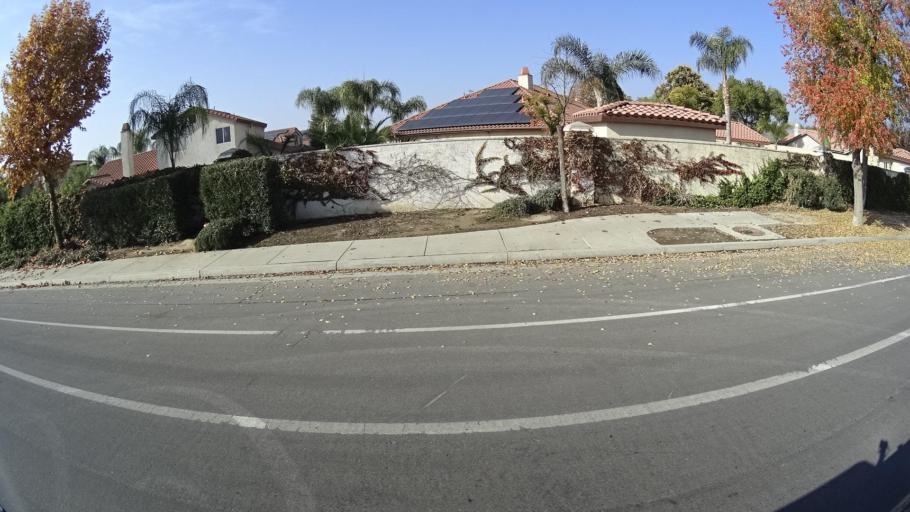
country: US
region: California
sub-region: Kern County
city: Delano
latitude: 35.7885
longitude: -119.2232
